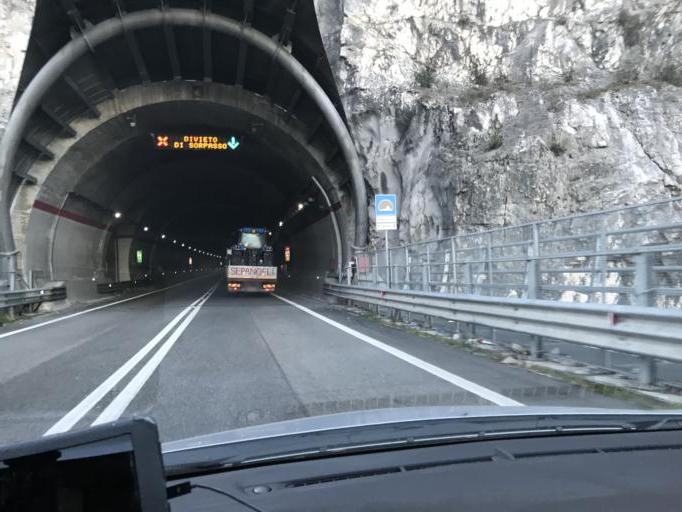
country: IT
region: Umbria
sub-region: Provincia di Terni
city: Terni
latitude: 42.5523
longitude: 12.7019
